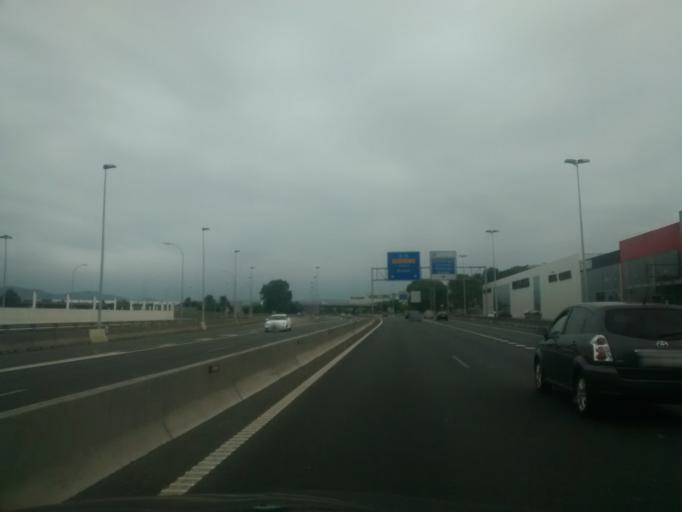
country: ES
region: Cantabria
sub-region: Provincia de Cantabria
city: Santander
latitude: 43.4438
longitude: -3.8347
